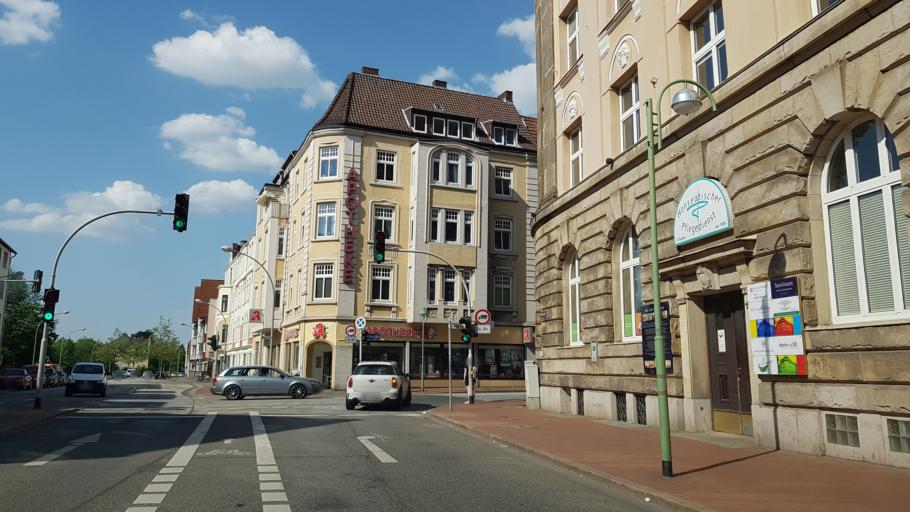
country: DE
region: Bremen
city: Bremerhaven
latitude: 53.5634
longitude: 8.5861
